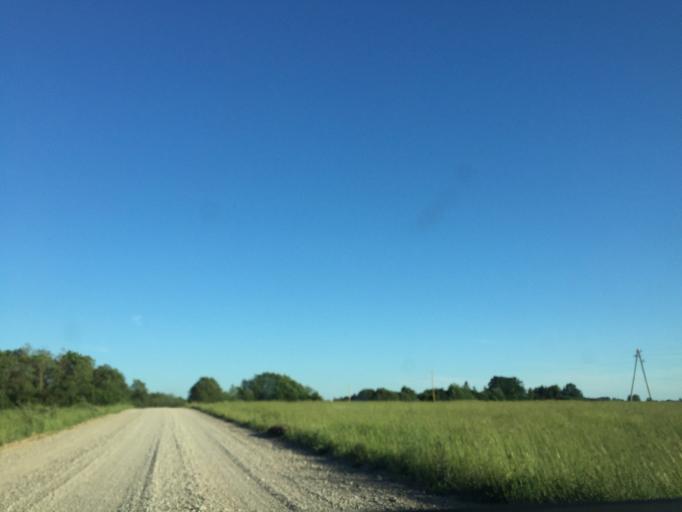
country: LV
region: Broceni
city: Broceni
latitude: 56.7932
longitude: 22.5530
